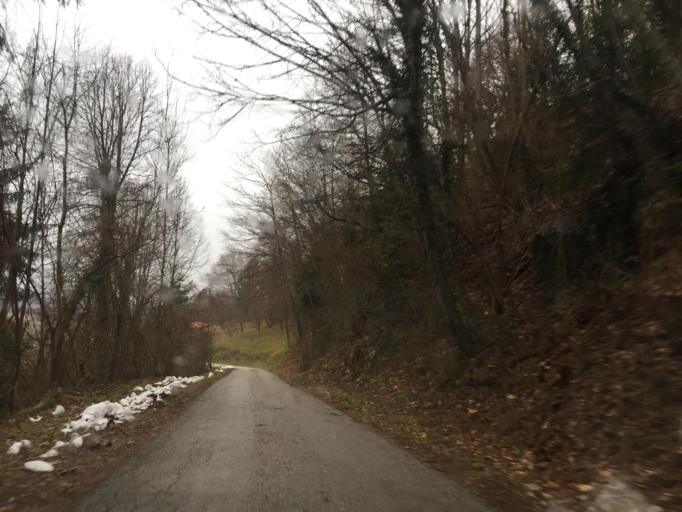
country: SI
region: Kanal
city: Kanal
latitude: 46.0755
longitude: 13.6714
